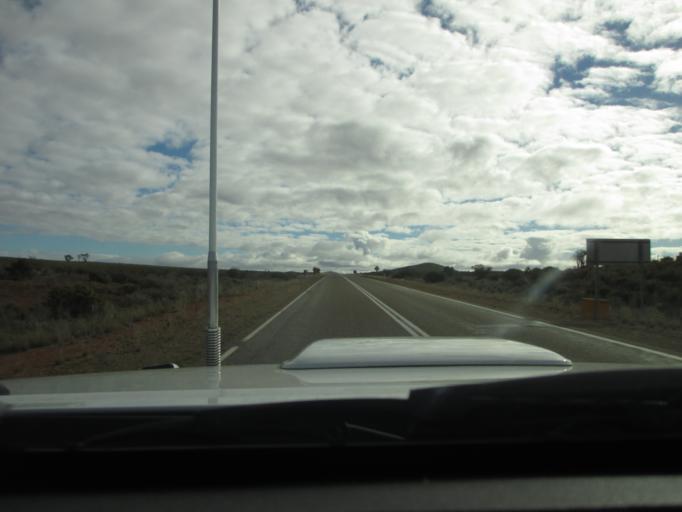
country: AU
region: South Australia
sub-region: Flinders Ranges
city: Quorn
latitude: -32.3079
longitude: 138.4854
